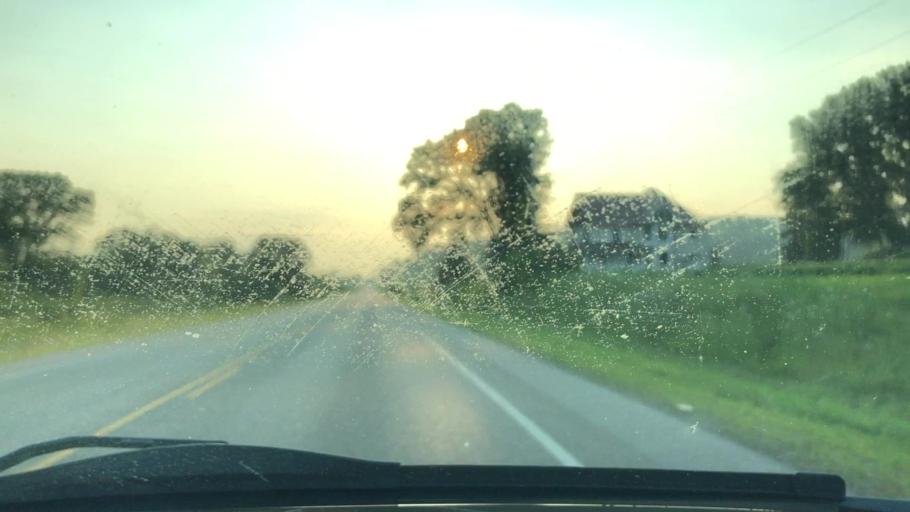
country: US
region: Wisconsin
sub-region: Dane County
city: Cross Plains
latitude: 43.1169
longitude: -89.6740
